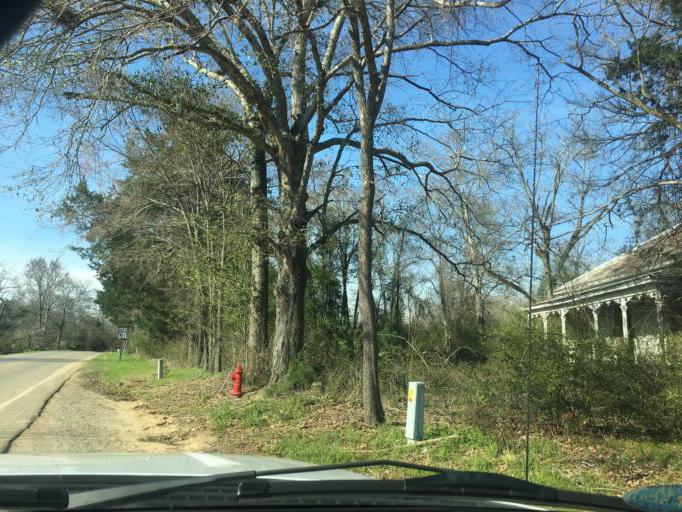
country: US
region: Alabama
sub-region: Lee County
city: Opelika
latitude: 32.4395
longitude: -85.3641
